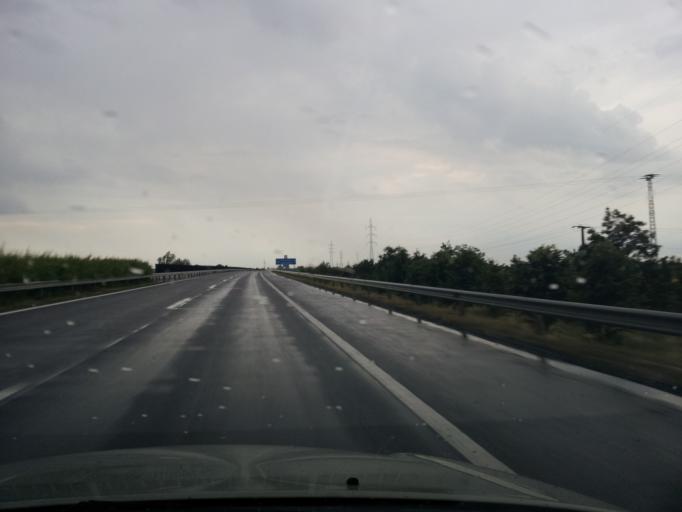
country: HU
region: Borsod-Abauj-Zemplen
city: Onod
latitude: 47.9971
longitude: 20.8903
